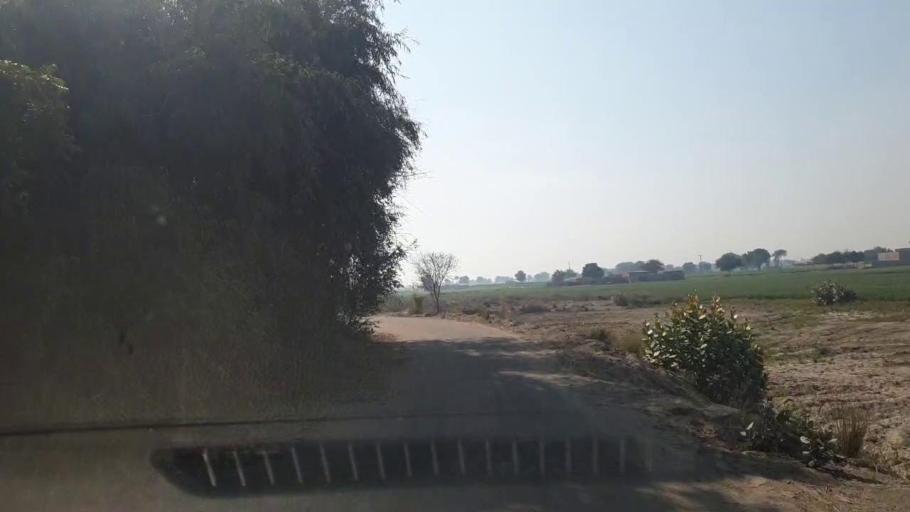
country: PK
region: Sindh
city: Shahpur Chakar
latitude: 26.1084
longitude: 68.6008
